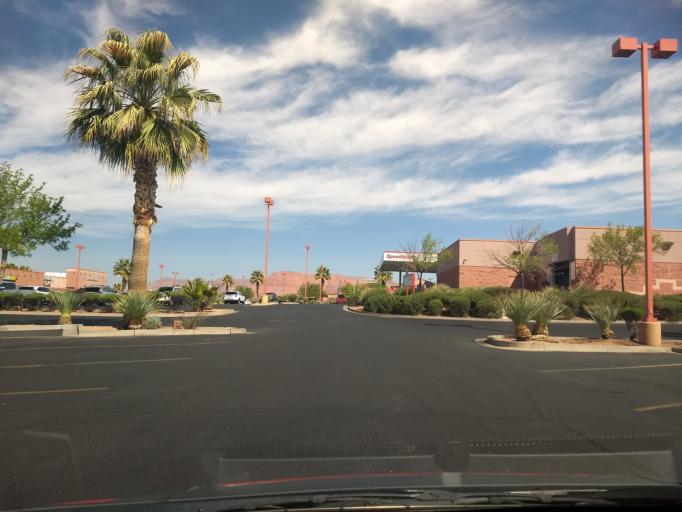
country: US
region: Utah
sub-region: Washington County
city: Santa Clara
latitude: 37.1219
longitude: -113.6248
